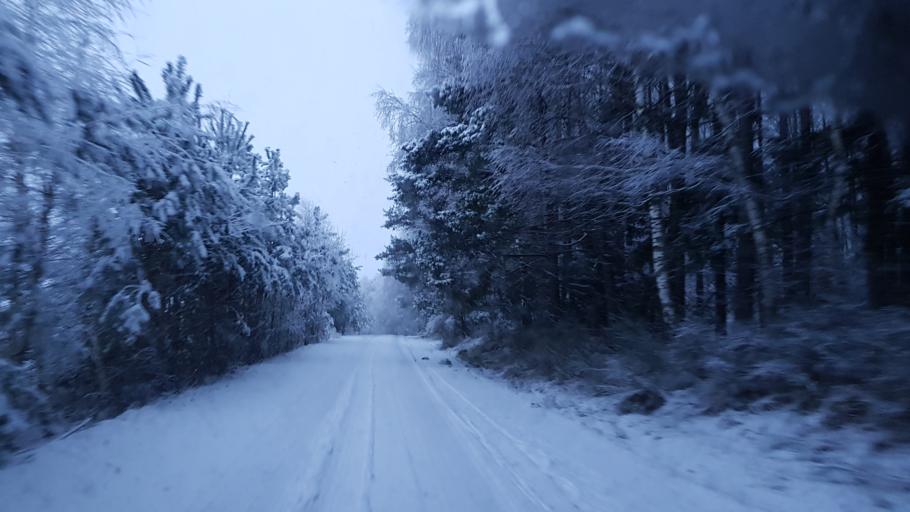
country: PL
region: West Pomeranian Voivodeship
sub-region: Powiat koszalinski
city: Sianow
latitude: 54.1663
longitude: 16.4662
